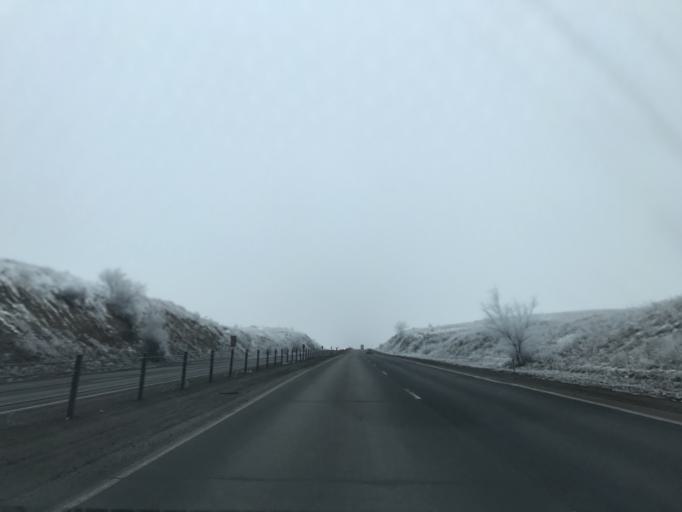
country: RU
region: Rostov
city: Likhoy
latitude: 48.1445
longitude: 40.2601
